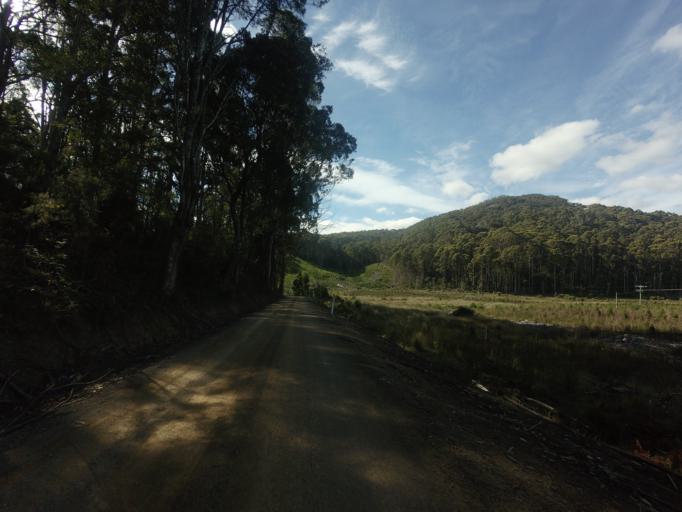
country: AU
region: Tasmania
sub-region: Clarence
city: Sandford
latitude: -43.1754
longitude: 147.7709
